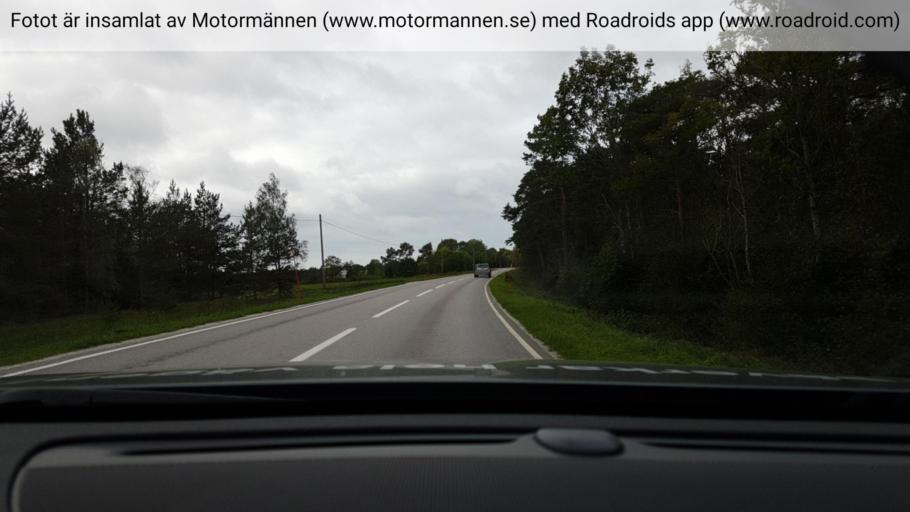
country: SE
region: Gotland
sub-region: Gotland
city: Klintehamn
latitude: 57.3187
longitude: 18.1820
